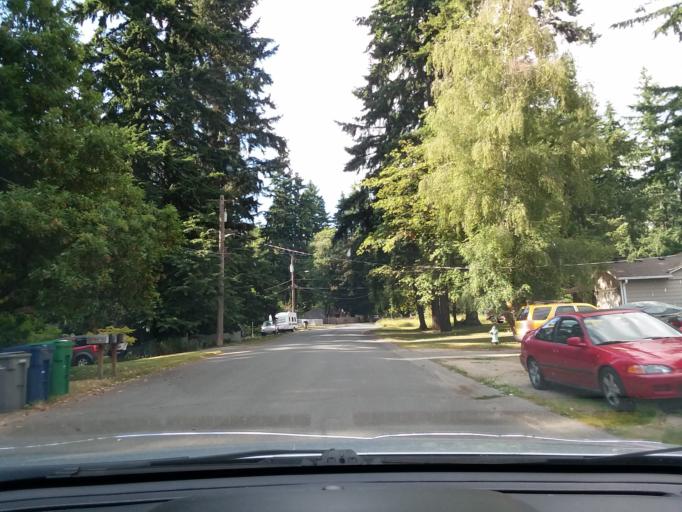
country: US
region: Washington
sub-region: Snohomish County
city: Mountlake Terrace
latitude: 47.7895
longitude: -122.3205
